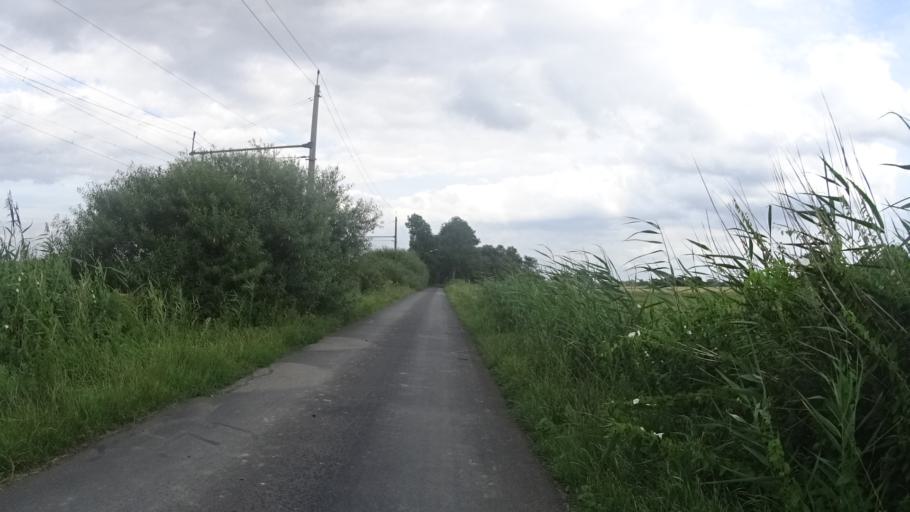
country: DE
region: Schleswig-Holstein
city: Gluckstadt
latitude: 53.7830
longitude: 9.4442
